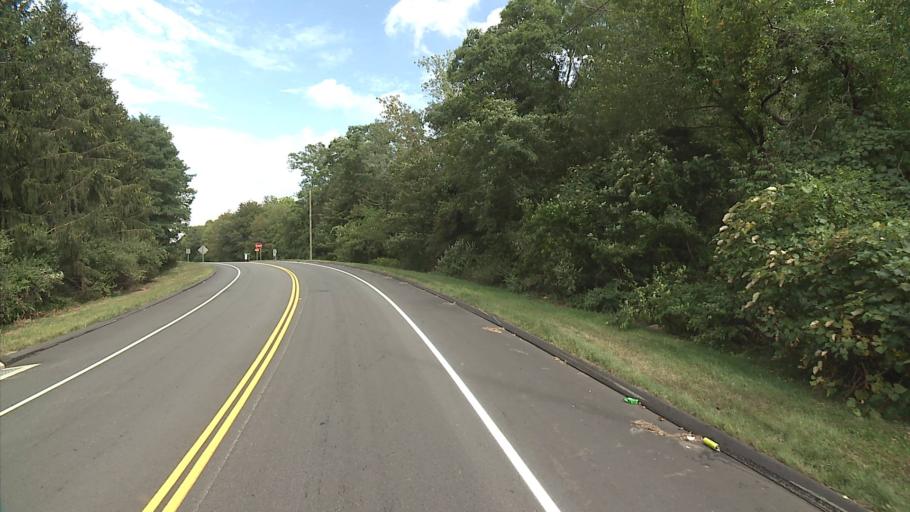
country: US
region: Connecticut
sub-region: New London County
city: Colchester
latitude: 41.5613
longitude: -72.3162
